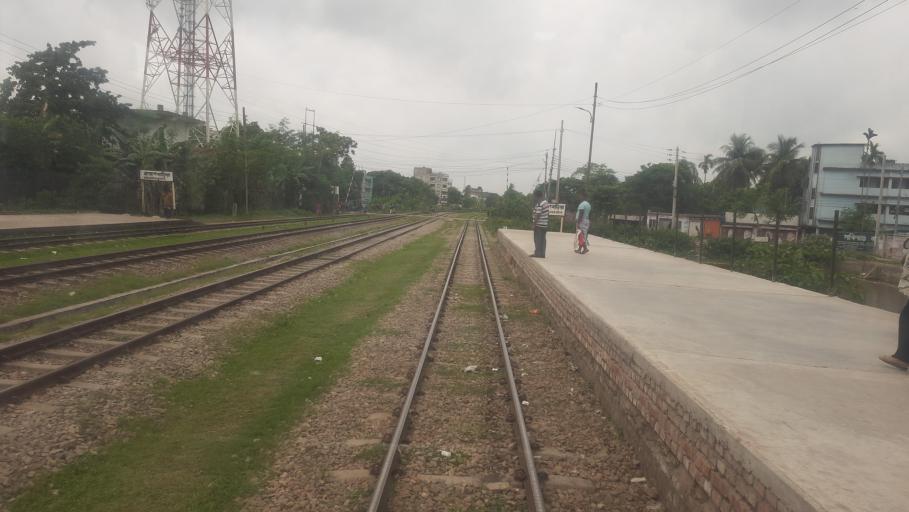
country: BD
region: Dhaka
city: Bhairab Bazar
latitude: 23.9661
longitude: 91.1069
